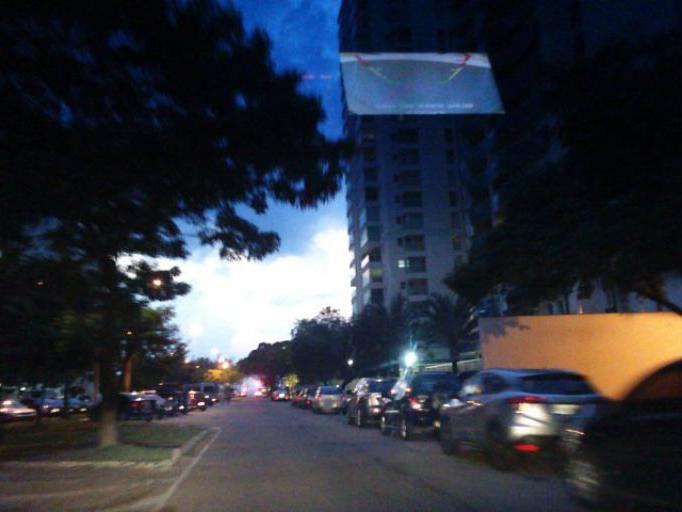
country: BR
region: Sao Paulo
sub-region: Sao Jose Dos Campos
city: Sao Jose dos Campos
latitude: -23.2173
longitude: -45.9079
